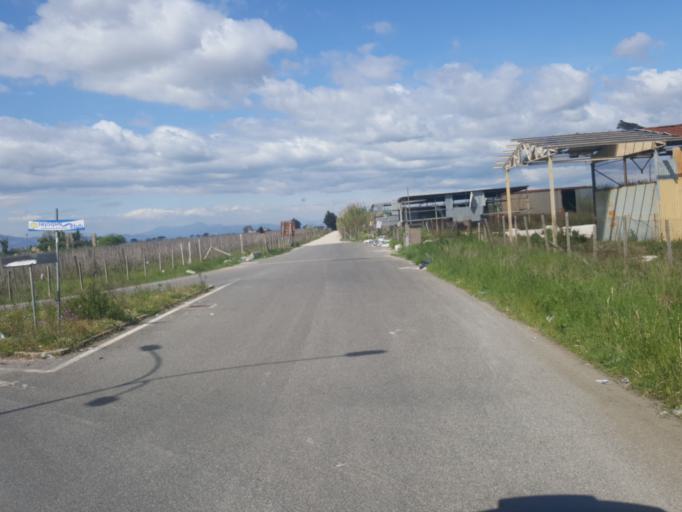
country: IT
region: Campania
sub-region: Provincia di Napoli
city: Amodio-Massariola
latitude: 40.9341
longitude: 14.0800
